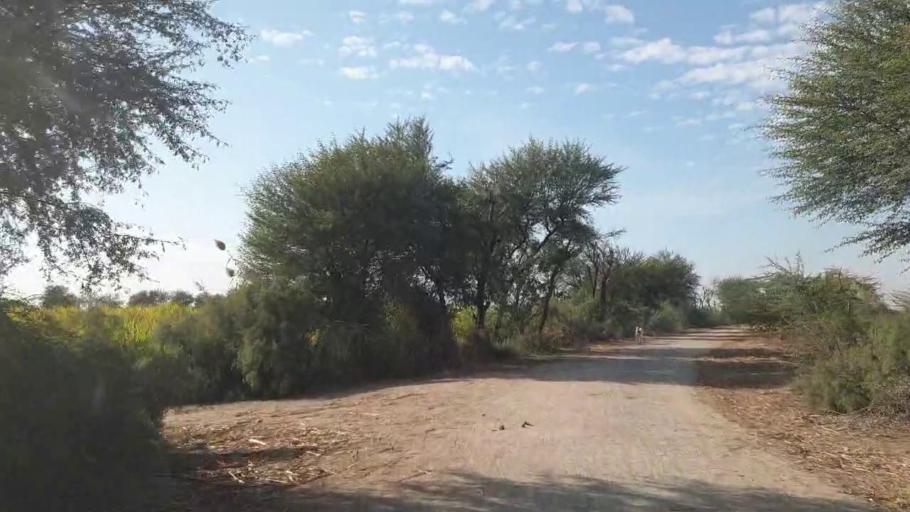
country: PK
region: Sindh
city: Sanghar
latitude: 26.0719
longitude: 68.8789
